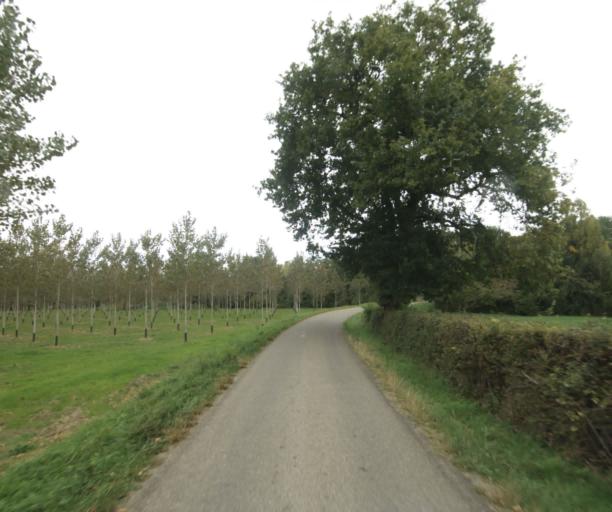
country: FR
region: Midi-Pyrenees
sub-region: Departement du Gers
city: Eauze
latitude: 43.8974
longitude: 0.0832
